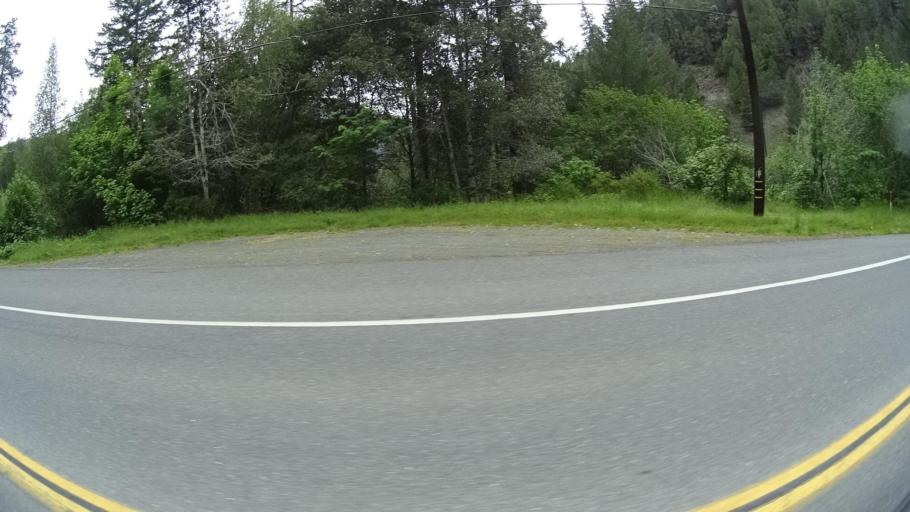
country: US
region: California
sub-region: Humboldt County
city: Willow Creek
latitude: 41.1233
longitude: -123.6846
